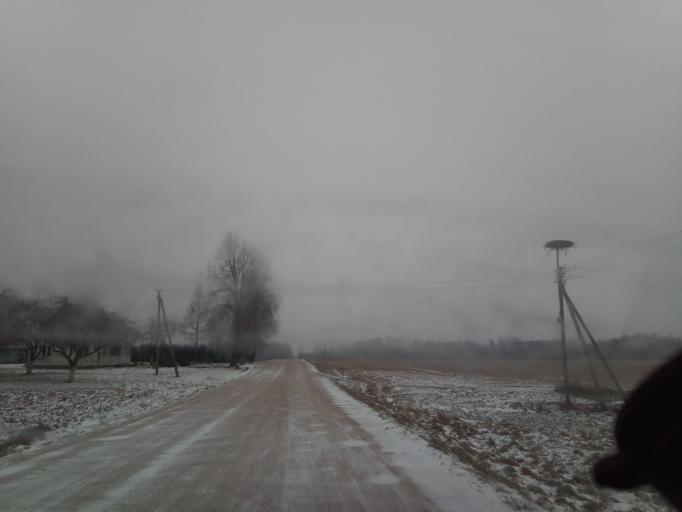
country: LT
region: Utenos apskritis
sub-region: Anyksciai
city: Anyksciai
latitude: 55.4469
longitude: 25.1030
